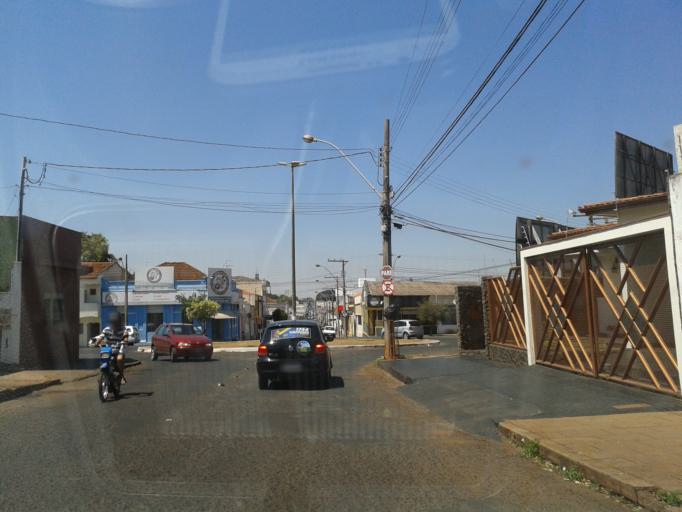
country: BR
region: Minas Gerais
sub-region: Araguari
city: Araguari
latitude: -18.6475
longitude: -48.1979
